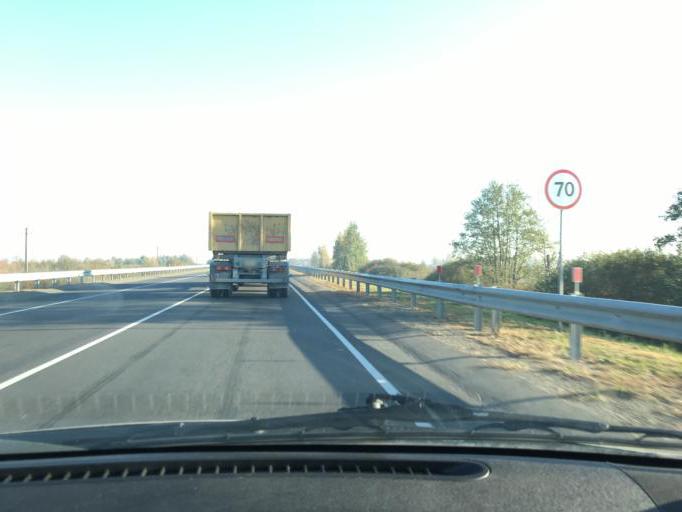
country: BY
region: Brest
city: Asnyezhytsy
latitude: 52.2098
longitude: 26.1204
